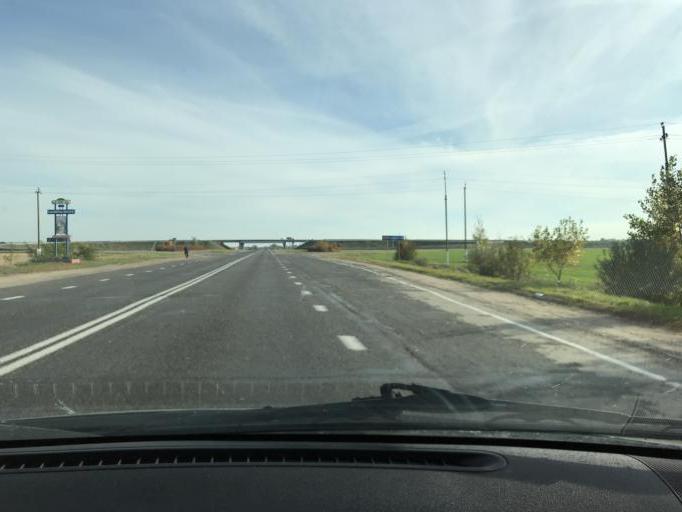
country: BY
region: Brest
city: Asnyezhytsy
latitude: 52.1882
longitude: 26.0766
